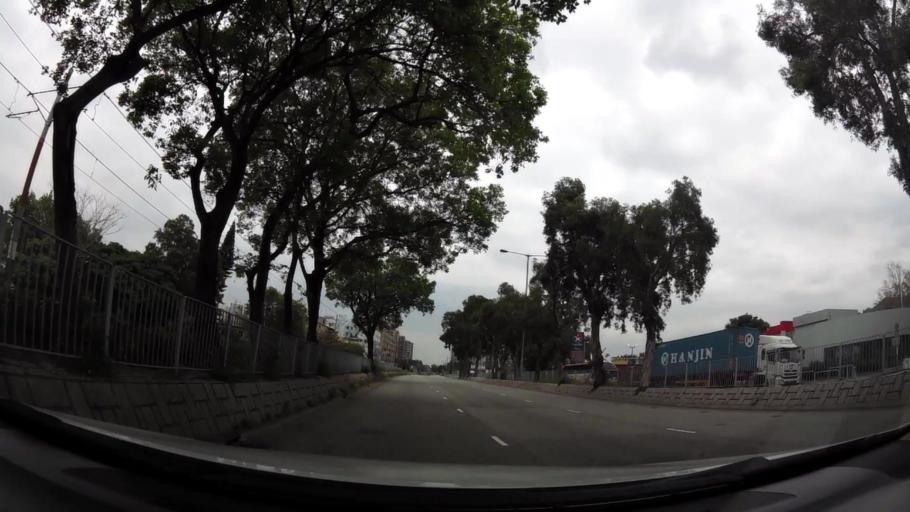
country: HK
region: Yuen Long
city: Yuen Long Kau Hui
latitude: 22.4312
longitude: 113.9943
